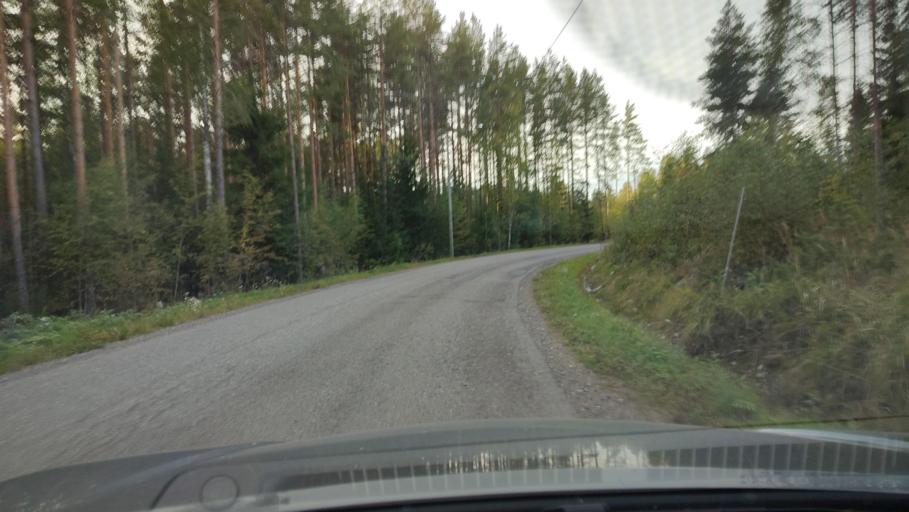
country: FI
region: Southern Ostrobothnia
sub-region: Suupohja
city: Karijoki
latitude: 62.1424
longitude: 21.5693
